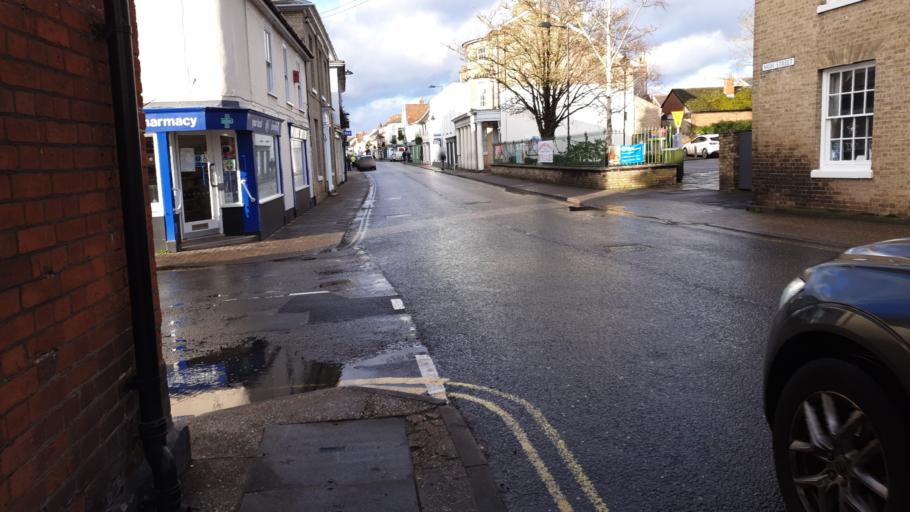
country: GB
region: England
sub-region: Suffolk
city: Hadleigh
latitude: 52.0426
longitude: 0.9548
